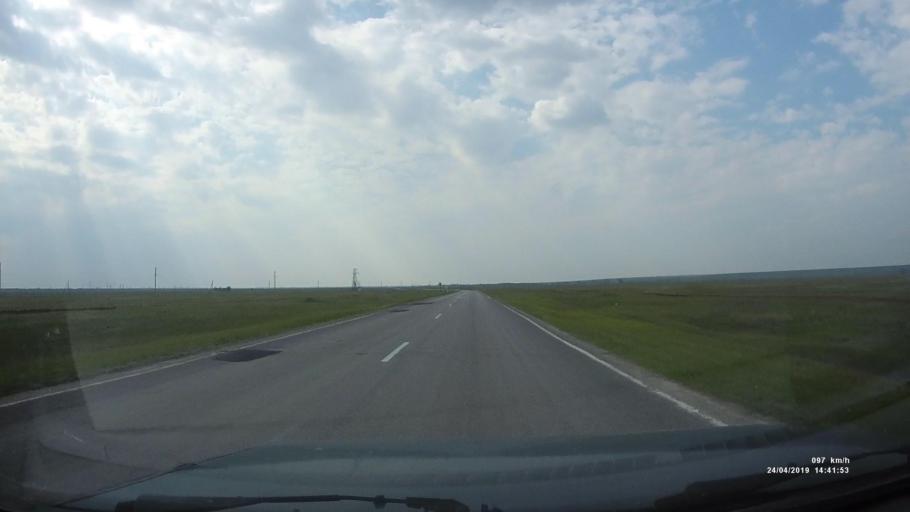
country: RU
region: Rostov
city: Remontnoye
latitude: 46.4488
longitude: 43.8726
